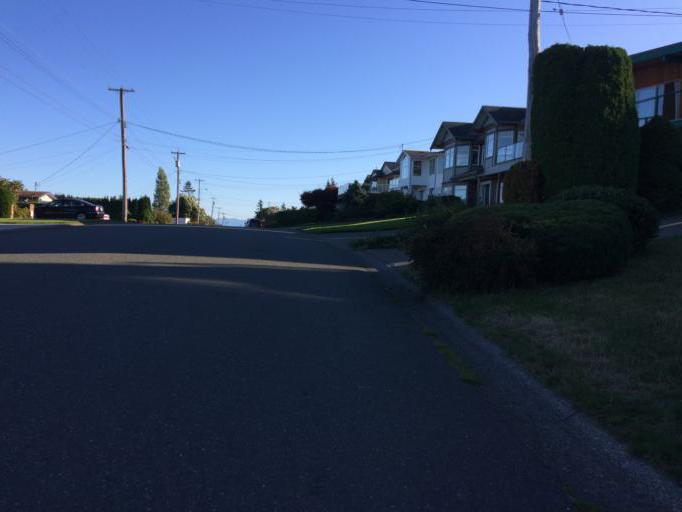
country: CA
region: British Columbia
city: Campbell River
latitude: 49.9960
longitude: -125.2338
